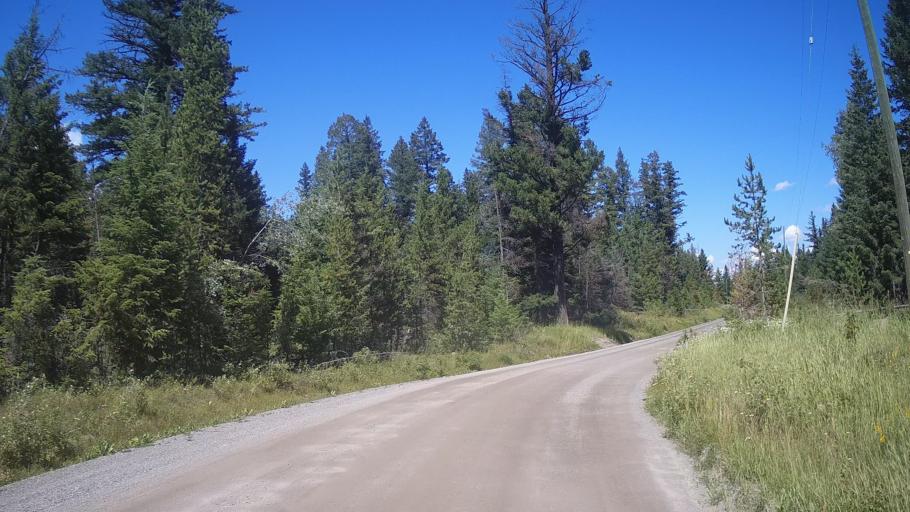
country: CA
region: British Columbia
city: Cache Creek
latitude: 51.1957
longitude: -121.5904
